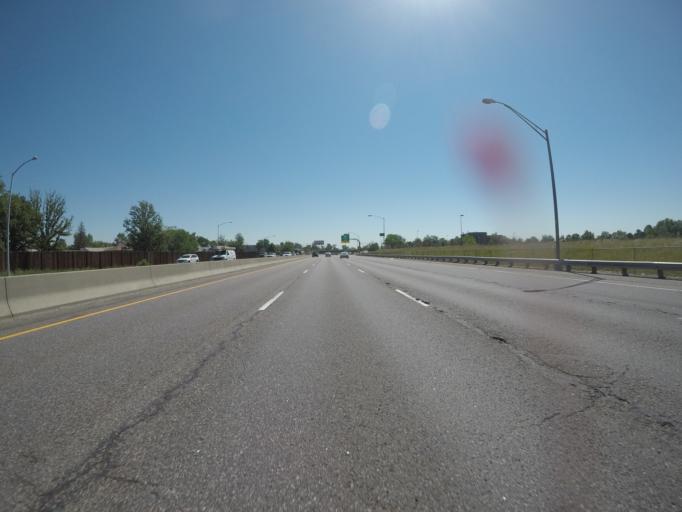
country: US
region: Colorado
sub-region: Adams County
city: Berkley
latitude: 39.7837
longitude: -105.0300
